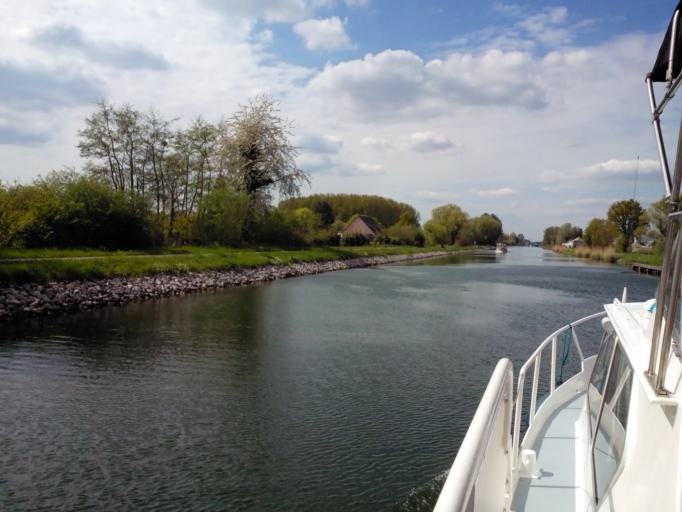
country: BE
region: Flanders
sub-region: Provincie Vlaams-Brabant
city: Boortmeerbeek
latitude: 50.9663
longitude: 4.5719
